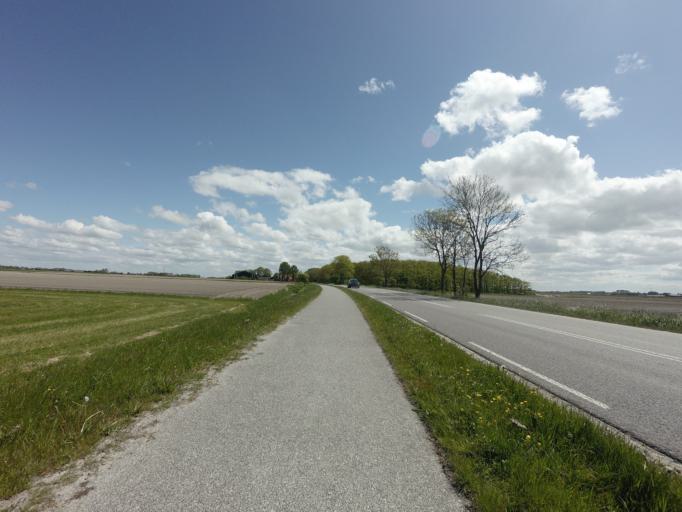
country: NL
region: Friesland
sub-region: Gemeente Harlingen
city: Harlingen
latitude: 53.1380
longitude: 5.4501
